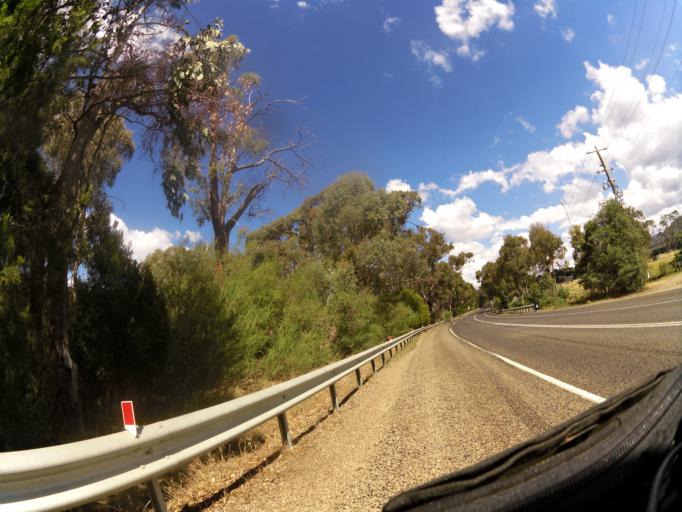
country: AU
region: Victoria
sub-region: Mansfield
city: Mansfield
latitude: -36.8296
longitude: 146.0086
